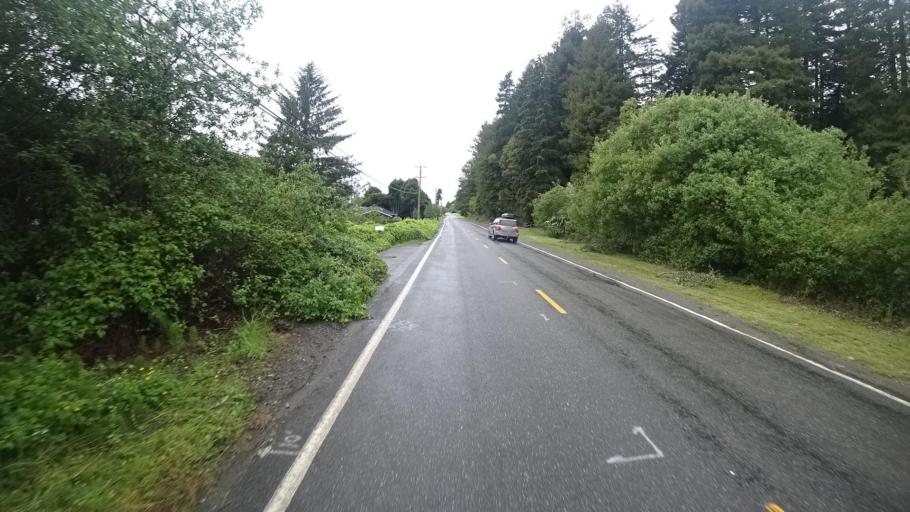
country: US
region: California
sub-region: Humboldt County
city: Bayside
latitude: 40.8336
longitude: -124.0451
